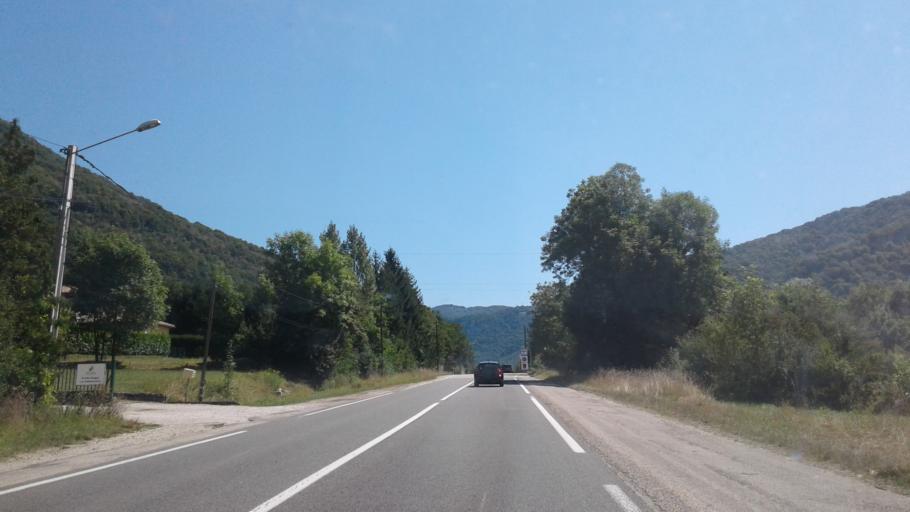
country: FR
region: Rhone-Alpes
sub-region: Departement de l'Ain
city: Vaux-en-Bugey
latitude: 45.9414
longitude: 5.3760
